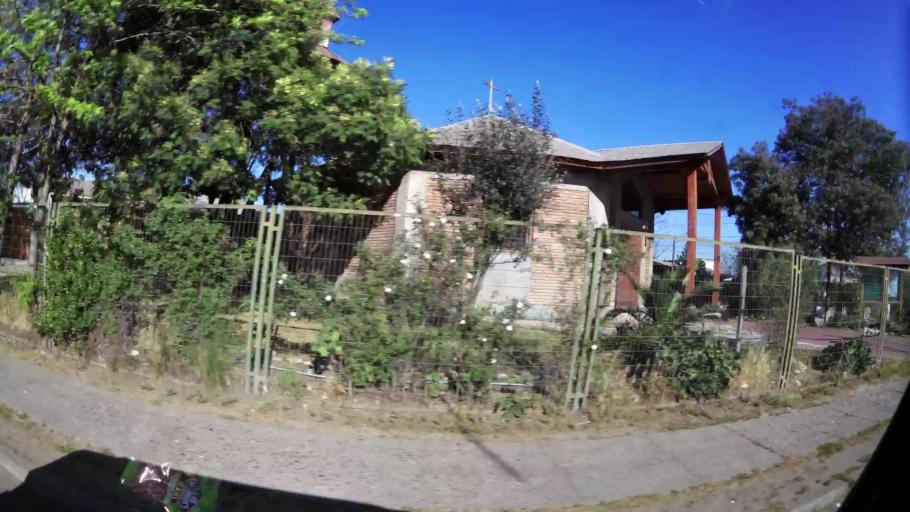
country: CL
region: Santiago Metropolitan
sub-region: Provincia de Talagante
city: Penaflor
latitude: -33.6129
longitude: -70.8725
